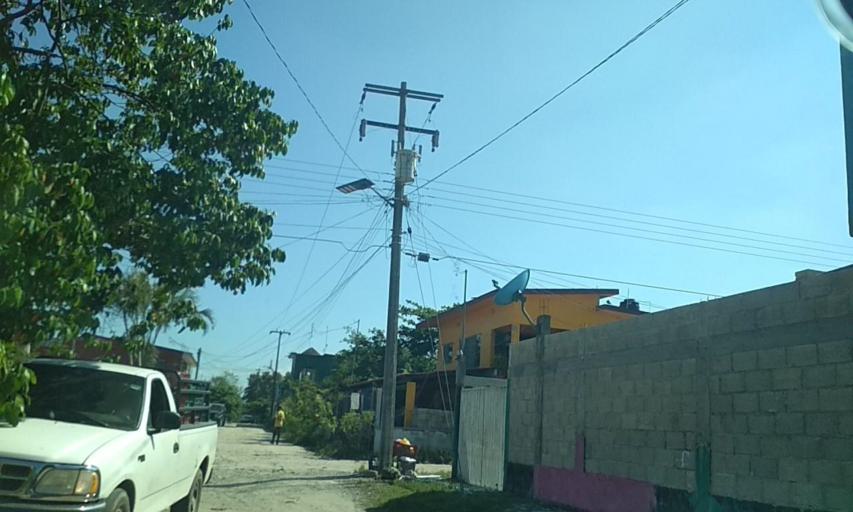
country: MX
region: Veracruz
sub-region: Martinez de la Torre
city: La Union Paso Largo
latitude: 20.1429
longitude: -97.0013
